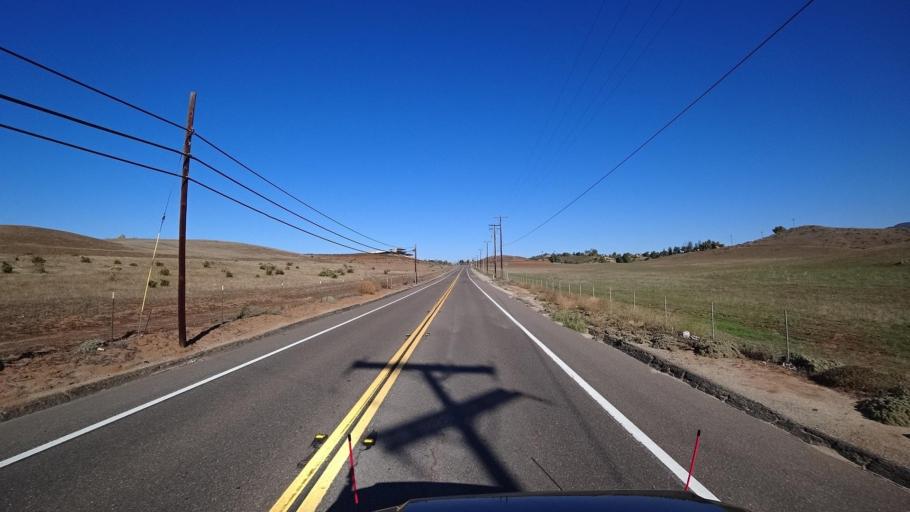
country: US
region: California
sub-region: San Diego County
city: Jamul
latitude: 32.6994
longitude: -116.8633
